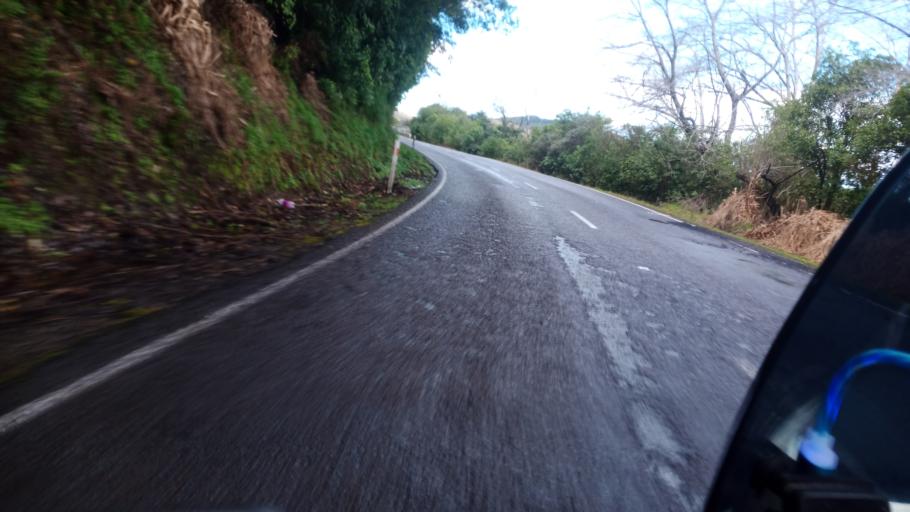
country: NZ
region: Gisborne
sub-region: Gisborne District
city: Gisborne
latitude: -37.8199
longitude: 178.3604
